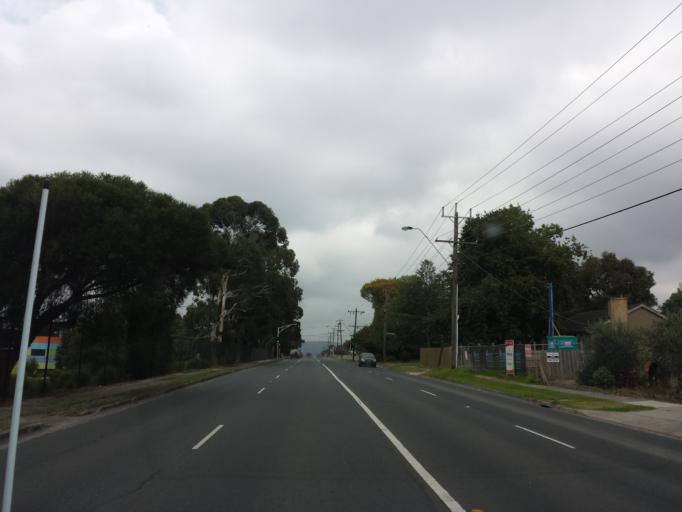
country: AU
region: Victoria
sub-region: Knox
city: Ferntree Gully
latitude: -37.8793
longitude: 145.2847
